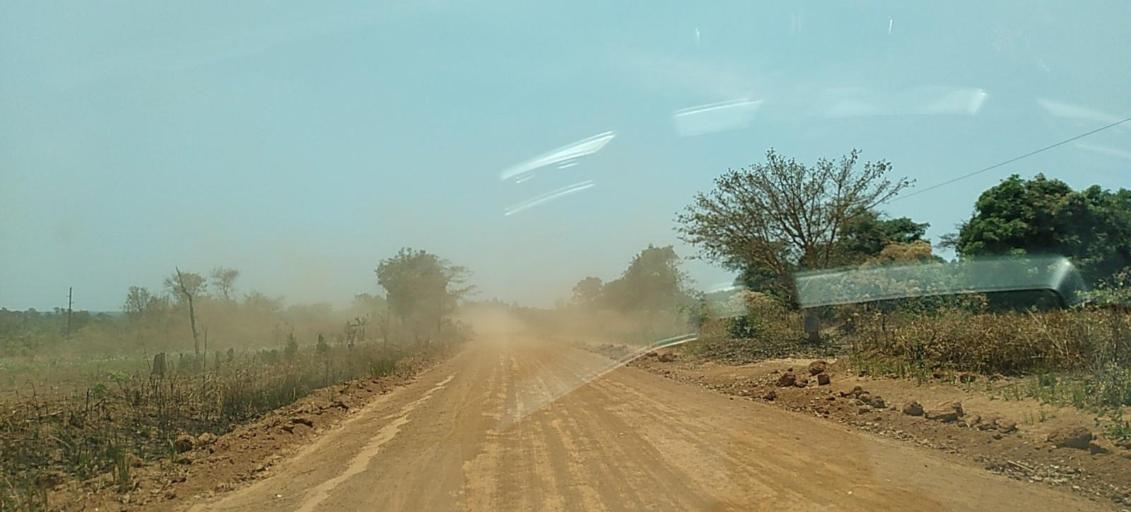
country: CD
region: Katanga
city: Kipushi
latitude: -11.8677
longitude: 27.1110
